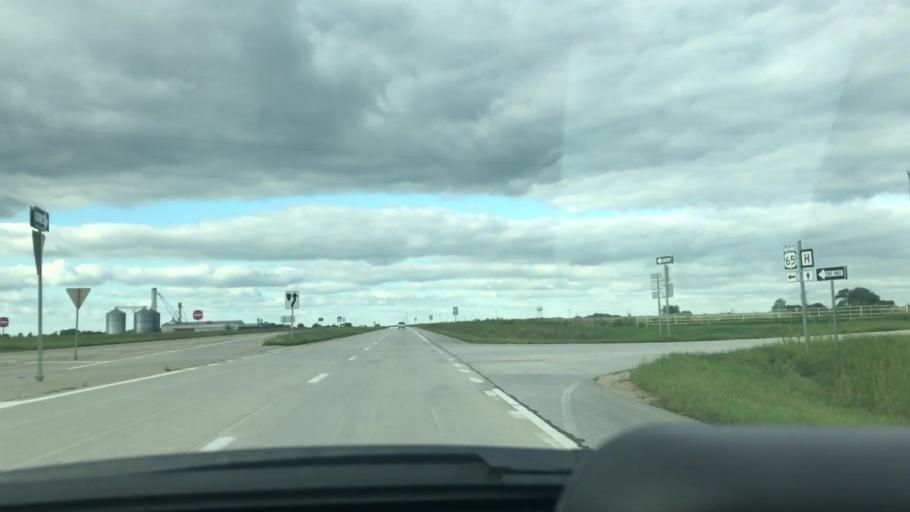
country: US
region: Missouri
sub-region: Benton County
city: Lincoln
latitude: 38.3766
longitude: -93.3371
